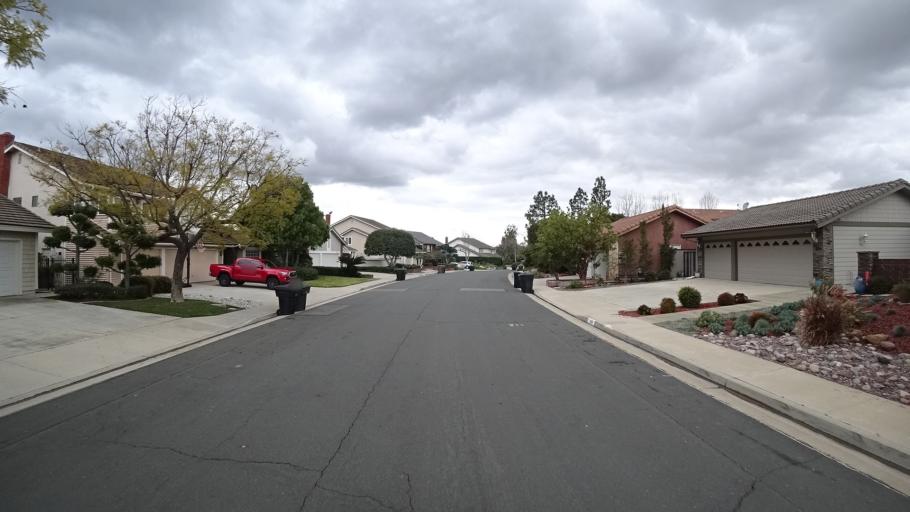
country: US
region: California
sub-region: Orange County
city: Villa Park
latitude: 33.8443
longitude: -117.7497
